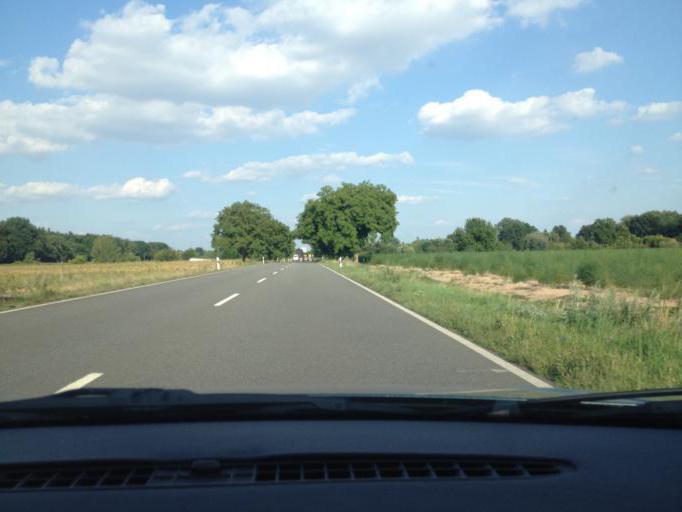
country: DE
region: Rheinland-Pfalz
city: Dudenhofen
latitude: 49.3182
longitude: 8.3740
